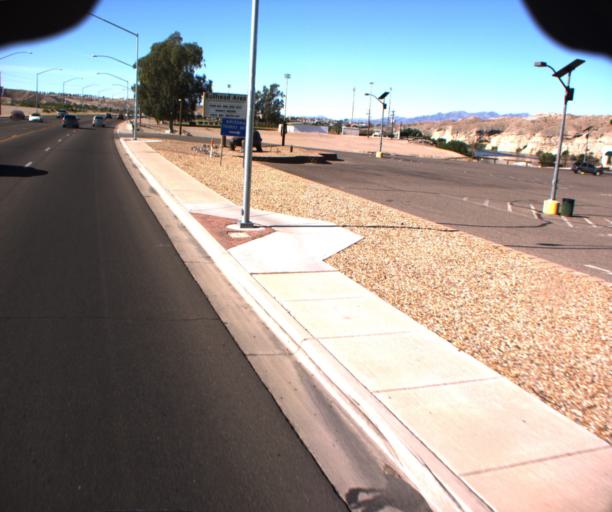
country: US
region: Arizona
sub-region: Mohave County
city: Bullhead City
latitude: 35.1390
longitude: -114.5700
